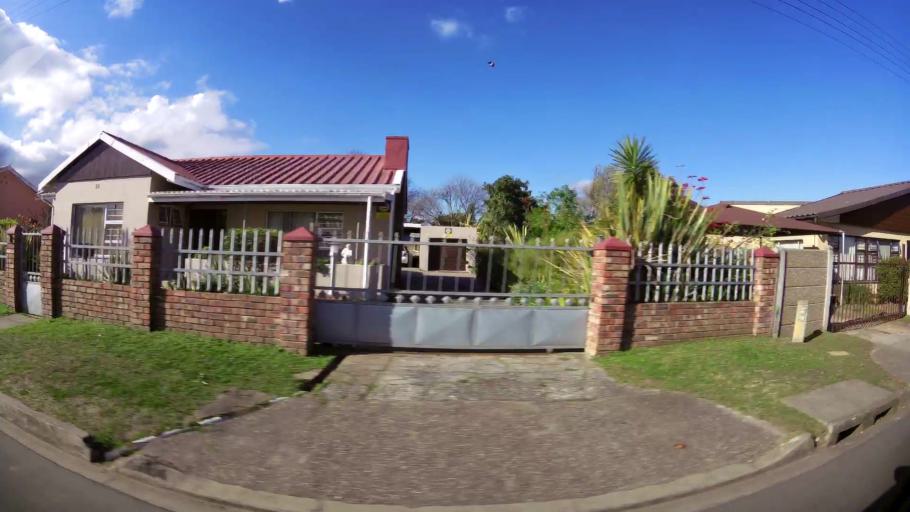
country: ZA
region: Western Cape
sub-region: Eden District Municipality
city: George
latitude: -33.9678
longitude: 22.4788
